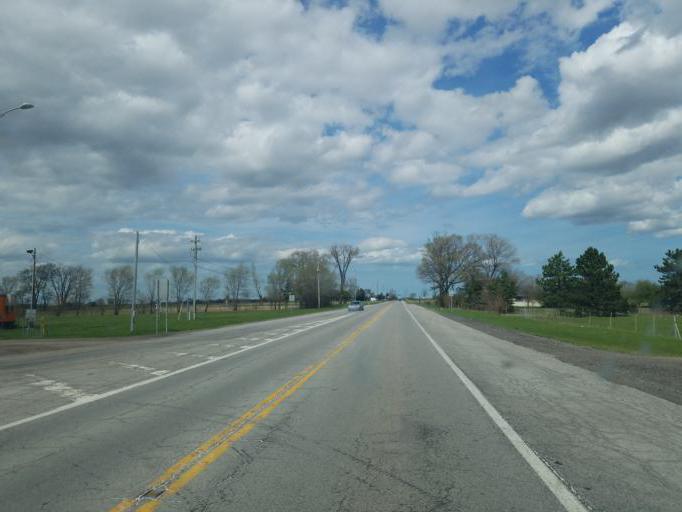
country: US
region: Ohio
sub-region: Huron County
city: Bellevue
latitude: 41.3424
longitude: -82.7584
